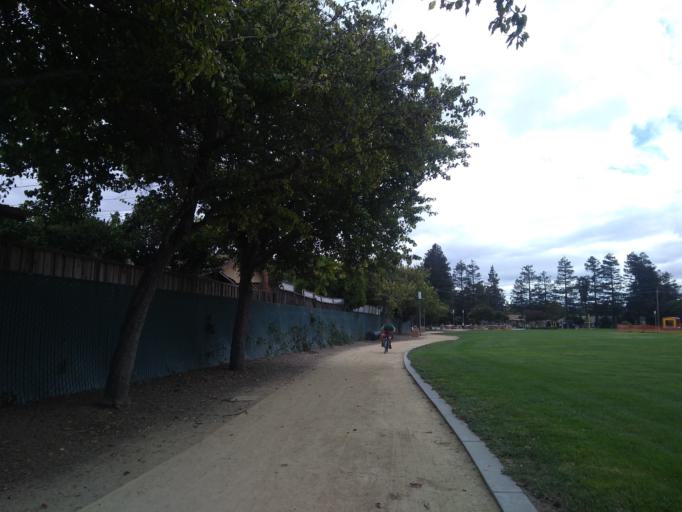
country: US
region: California
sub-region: Santa Clara County
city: Santa Clara
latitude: 37.3972
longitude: -121.9889
